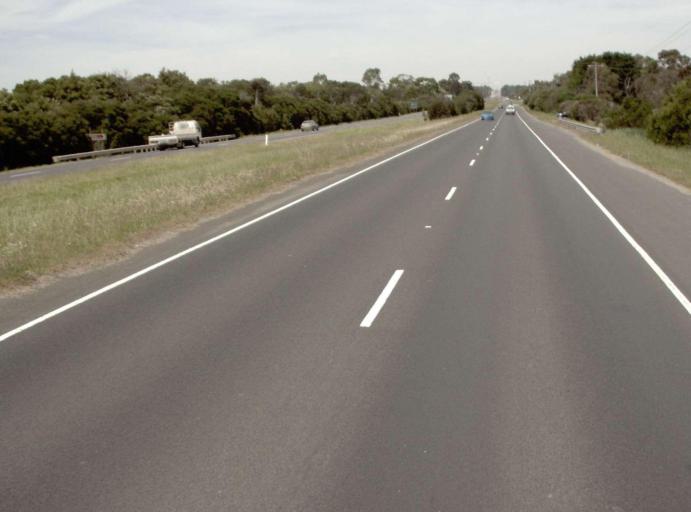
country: AU
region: Victoria
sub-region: Frankston
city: Skye
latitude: -38.1167
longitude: 145.2315
